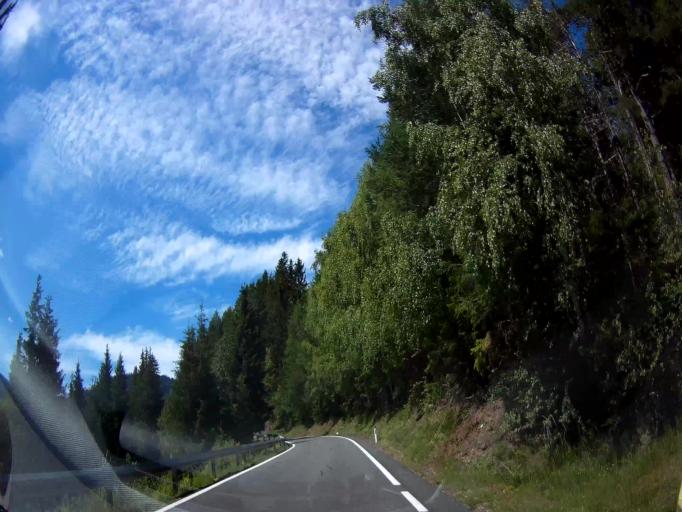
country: AT
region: Carinthia
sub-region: Politischer Bezirk Sankt Veit an der Glan
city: Glodnitz
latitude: 46.9189
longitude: 14.0603
